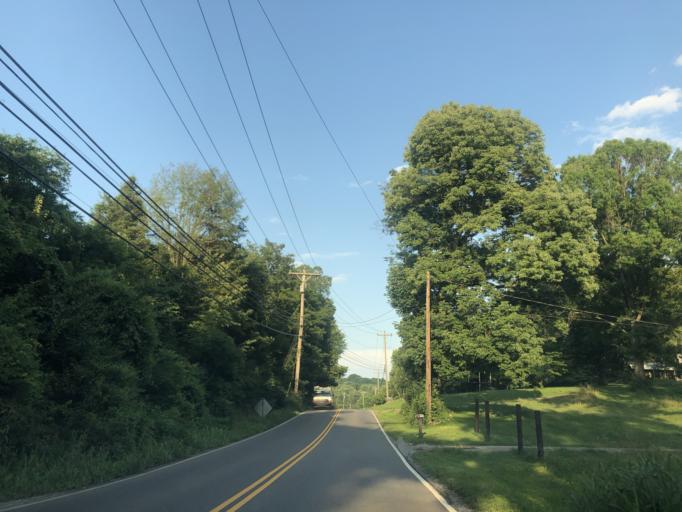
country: US
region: Tennessee
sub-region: Davidson County
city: Lakewood
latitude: 36.1423
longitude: -86.6450
